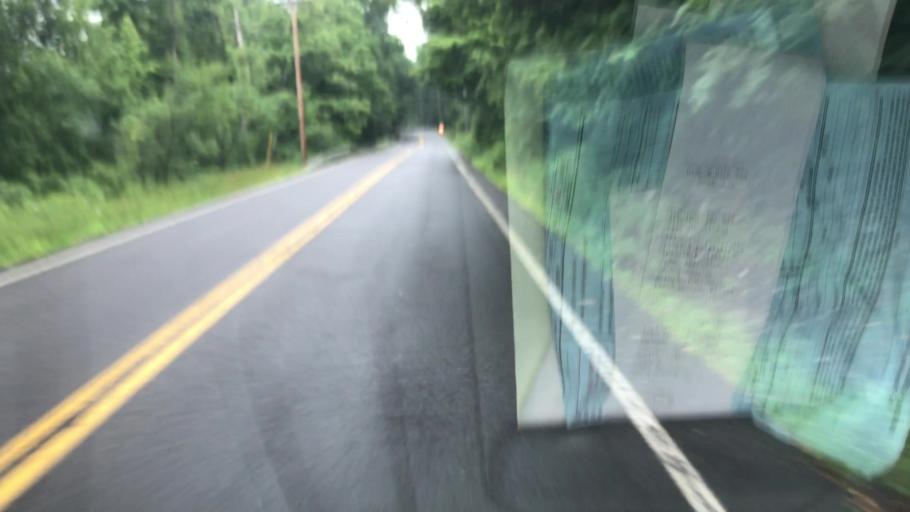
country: US
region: New York
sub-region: Onondaga County
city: Manlius
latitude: 43.0012
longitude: -75.9979
